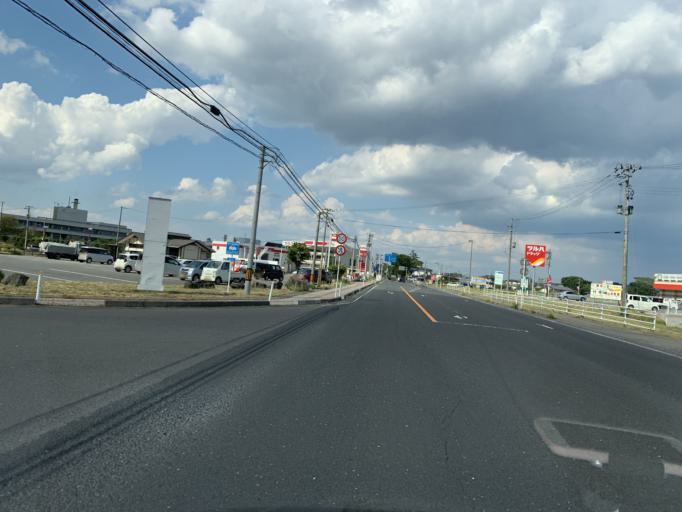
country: JP
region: Miyagi
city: Wakuya
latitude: 38.6269
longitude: 141.1890
